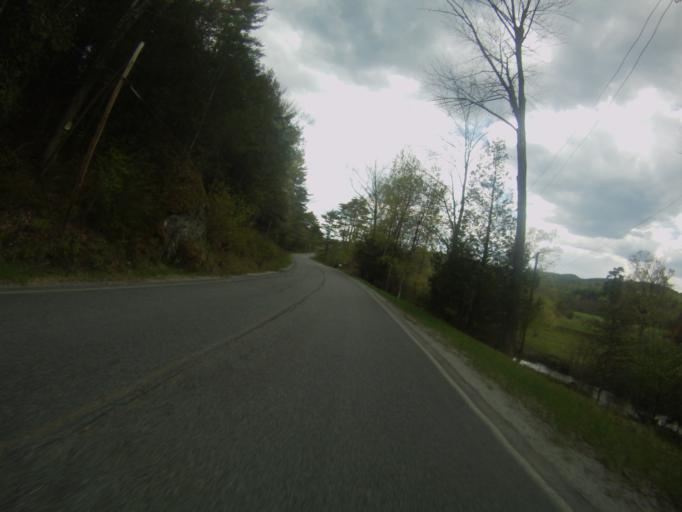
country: US
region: New York
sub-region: Essex County
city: Mineville
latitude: 44.0534
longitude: -73.5378
